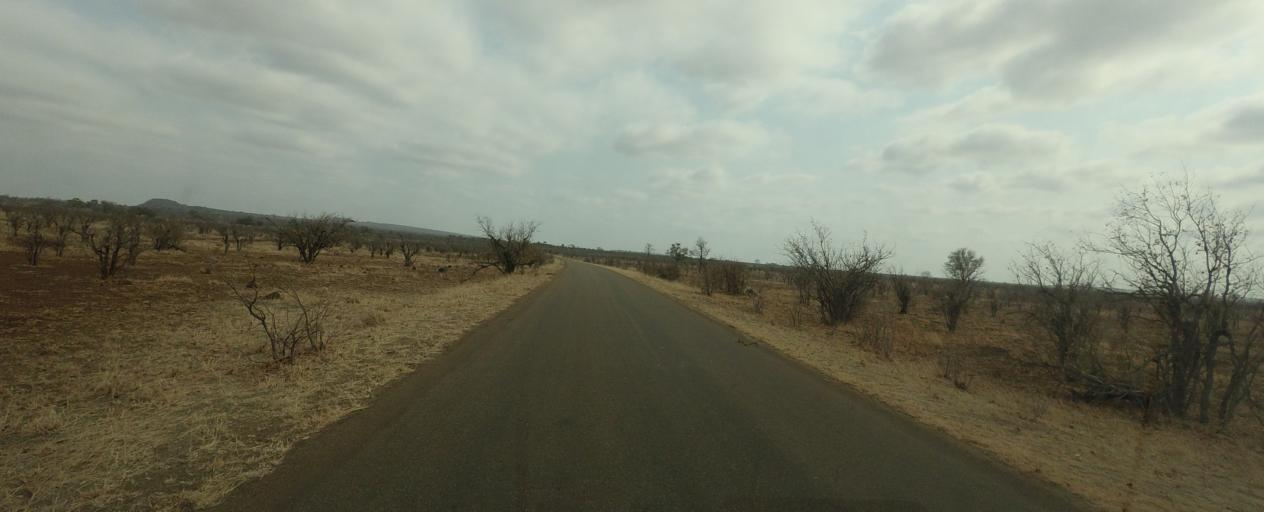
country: ZA
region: Limpopo
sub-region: Vhembe District Municipality
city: Mutale
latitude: -22.6304
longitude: 31.1799
